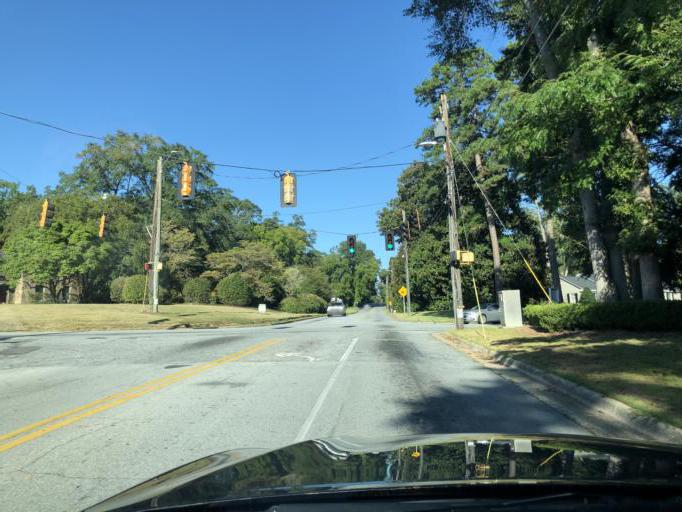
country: US
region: Georgia
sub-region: Muscogee County
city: Columbus
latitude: 32.4786
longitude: -84.9549
